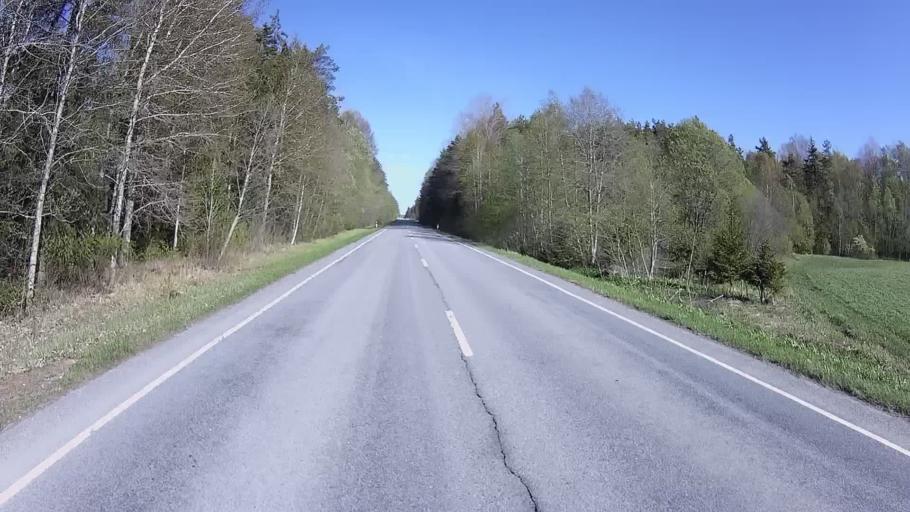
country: EE
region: Raplamaa
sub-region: Jaervakandi vald
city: Jarvakandi
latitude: 58.8499
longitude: 24.7950
